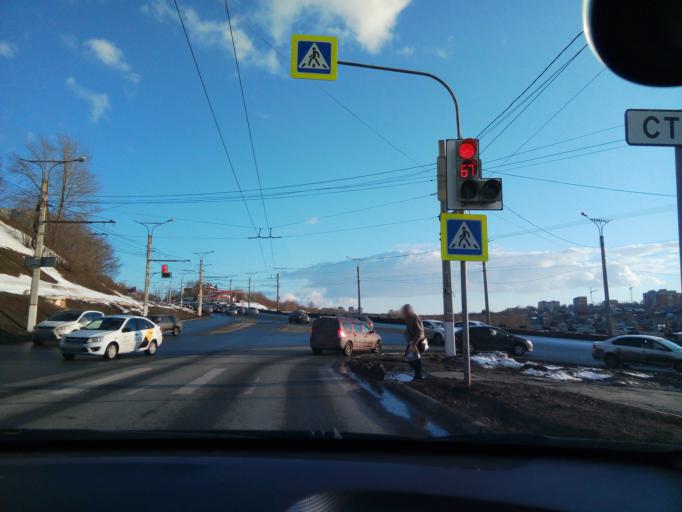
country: RU
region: Chuvashia
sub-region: Cheboksarskiy Rayon
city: Cheboksary
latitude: 56.1330
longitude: 47.2412
